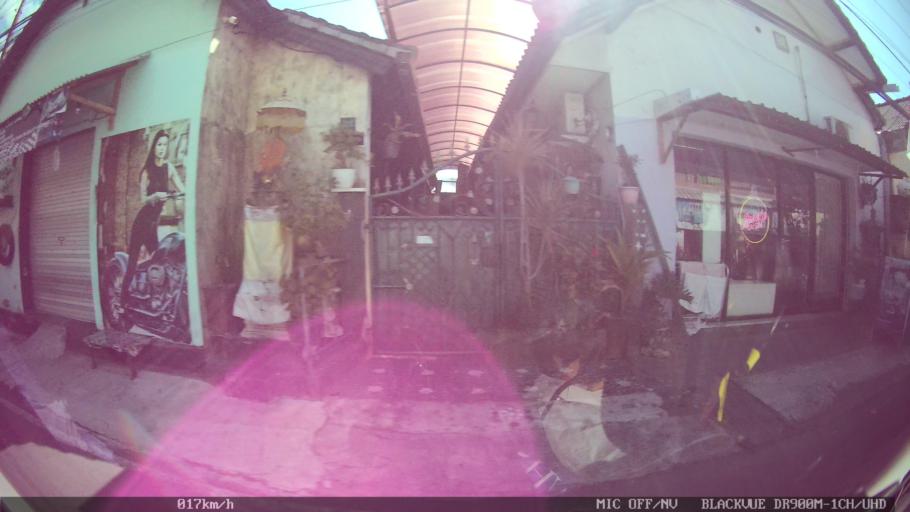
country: ID
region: Bali
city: Banjar Kertasari
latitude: -8.6454
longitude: 115.1797
